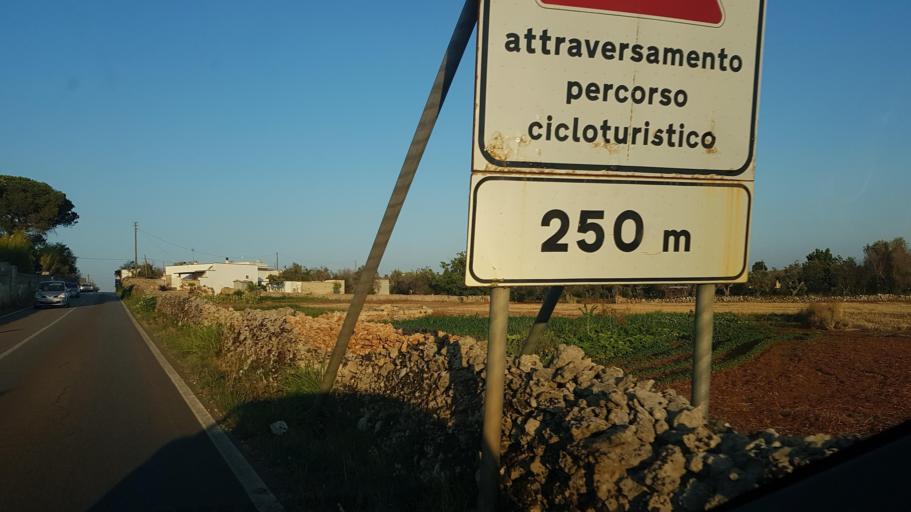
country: IT
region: Apulia
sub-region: Provincia di Lecce
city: Lucugnano
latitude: 39.9385
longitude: 18.3103
